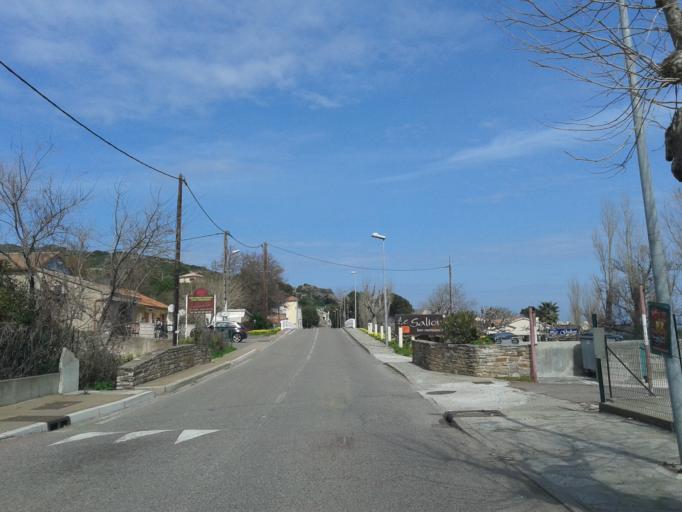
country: FR
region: Corsica
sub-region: Departement de la Haute-Corse
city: Brando
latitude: 42.8093
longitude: 9.4887
